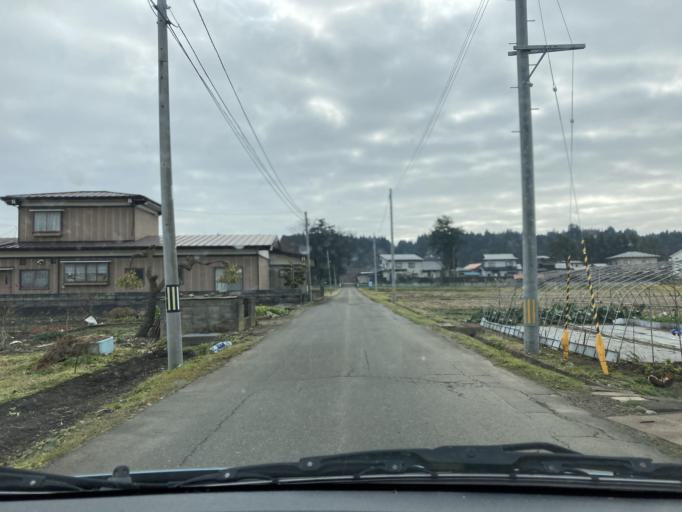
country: JP
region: Iwate
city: Kitakami
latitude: 39.2785
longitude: 141.0765
